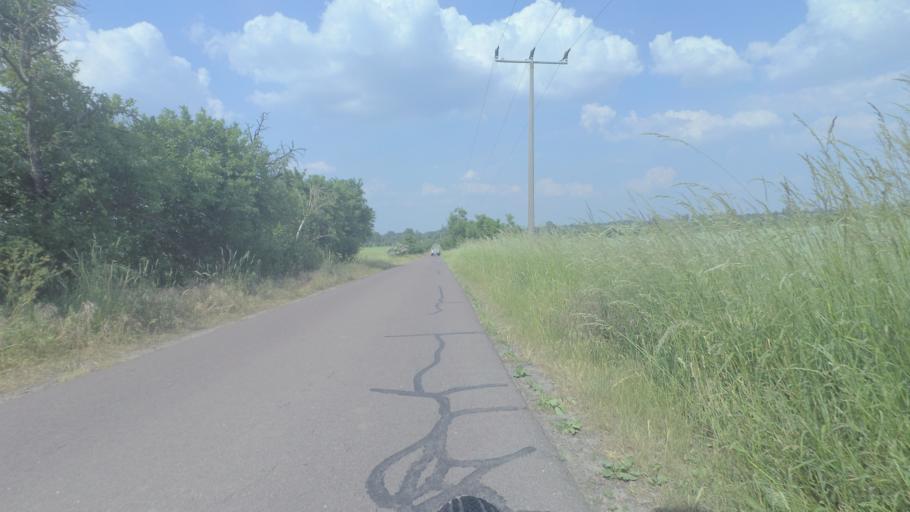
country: DE
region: Saxony-Anhalt
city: Koethen
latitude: 51.7670
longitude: 11.9212
